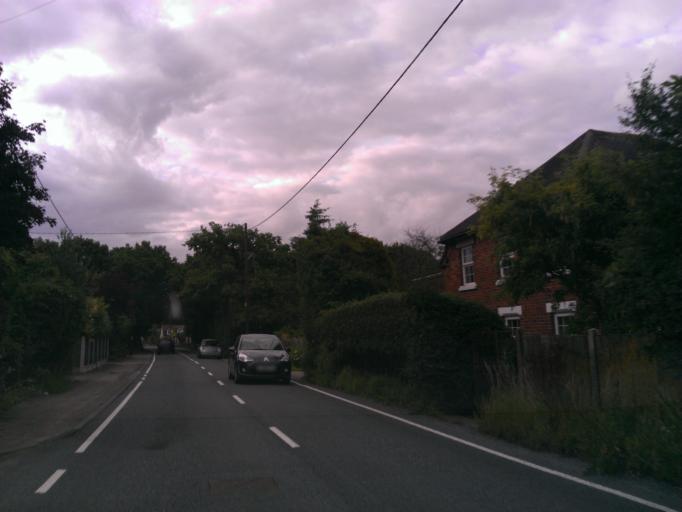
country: GB
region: England
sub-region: Essex
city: Alresford
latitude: 51.8627
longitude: 0.9956
